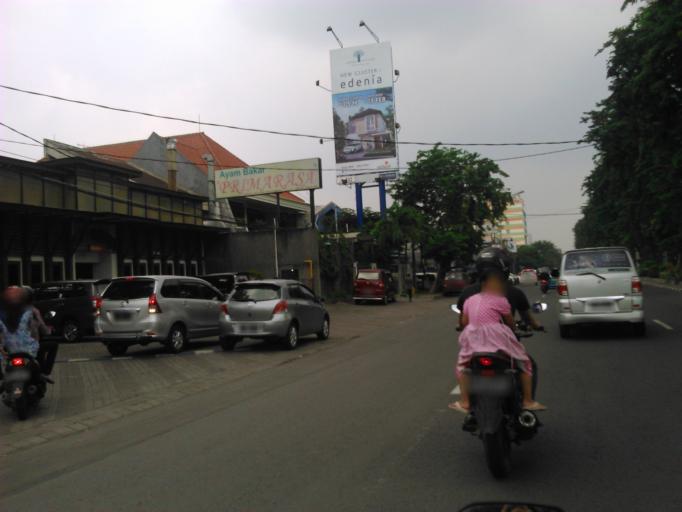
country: ID
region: East Java
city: Gubengairlangga
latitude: -7.2803
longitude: 112.7688
